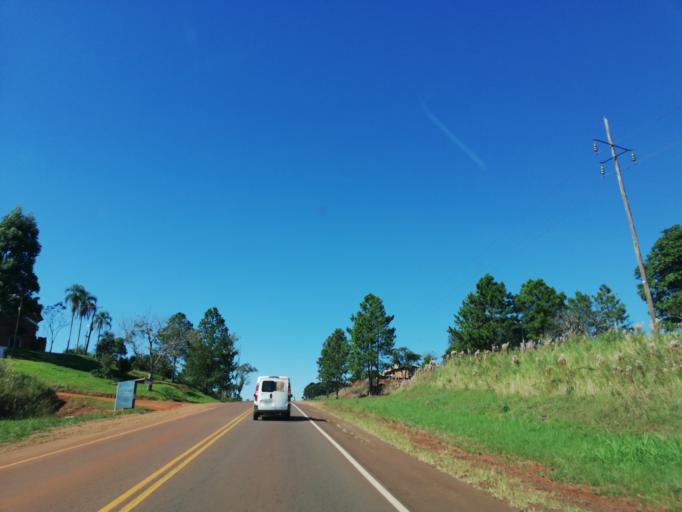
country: AR
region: Misiones
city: Dos de Mayo
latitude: -27.0583
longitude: -54.4287
